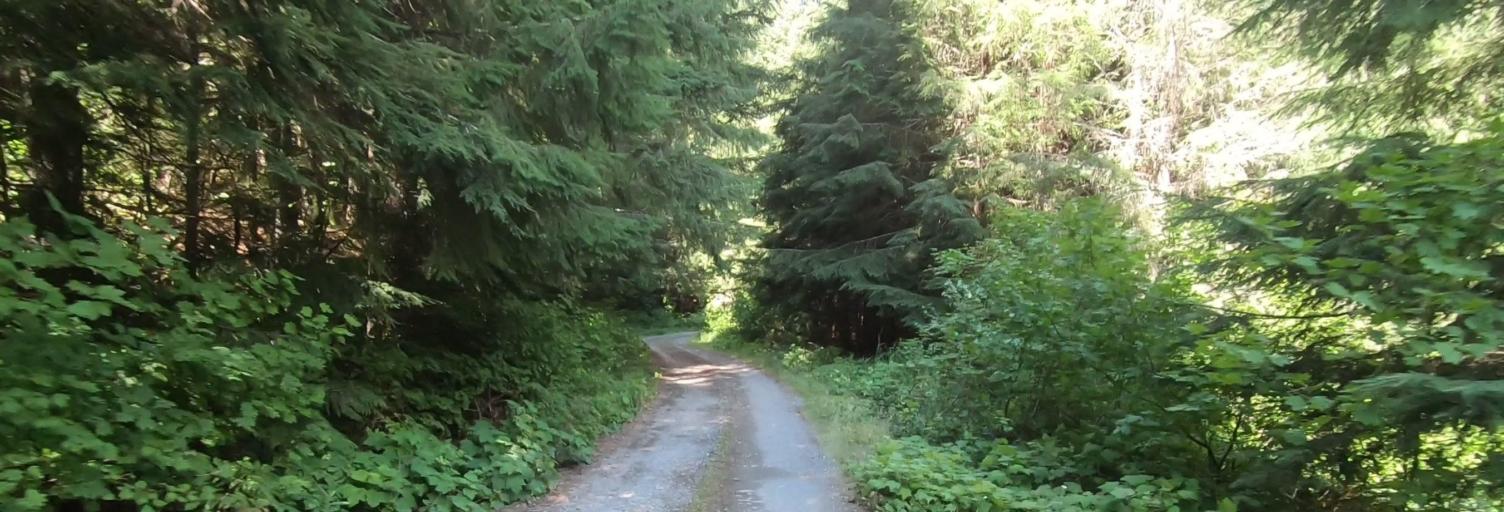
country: CA
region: British Columbia
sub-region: Fraser Valley Regional District
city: Chilliwack
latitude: 48.8610
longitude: -121.7747
